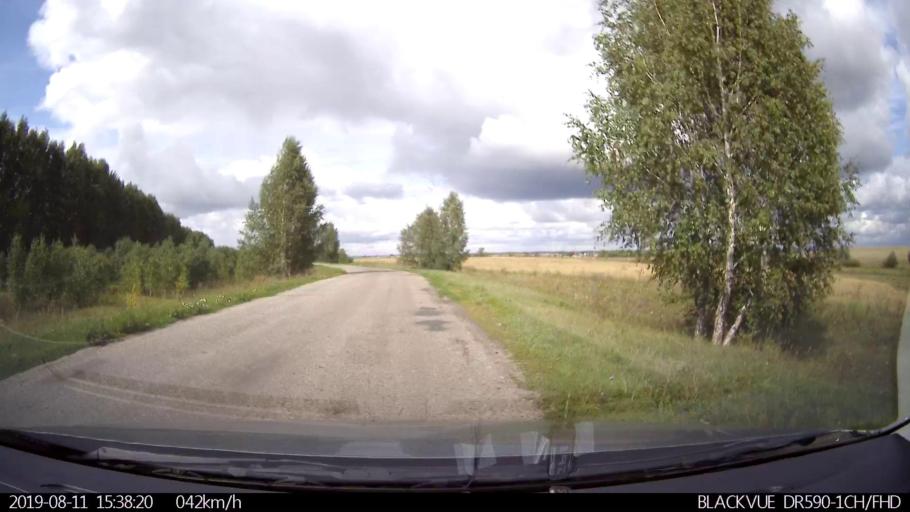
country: RU
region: Ulyanovsk
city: Ignatovka
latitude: 53.8607
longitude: 47.6407
